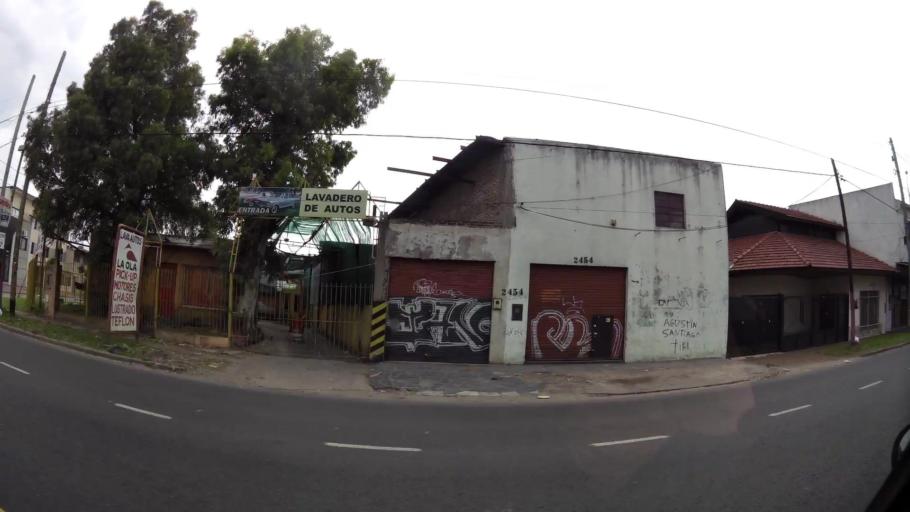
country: AR
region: Buenos Aires
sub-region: Partido de Quilmes
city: Quilmes
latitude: -34.7517
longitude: -58.2904
